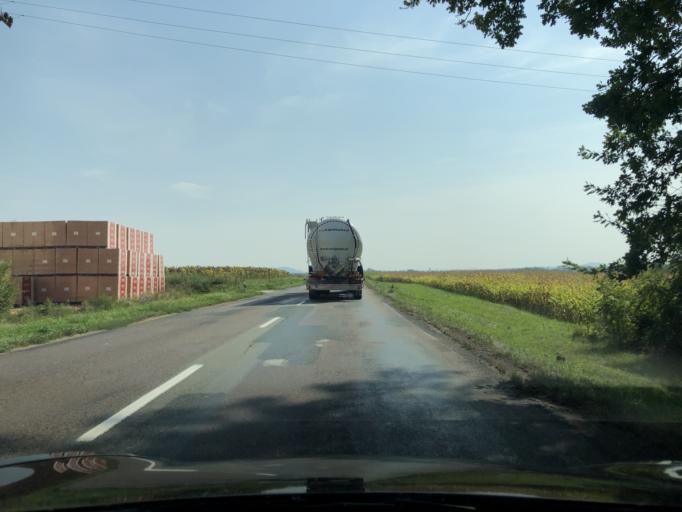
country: CZ
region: South Moravian
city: Novosedly
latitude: 48.8351
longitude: 16.5138
